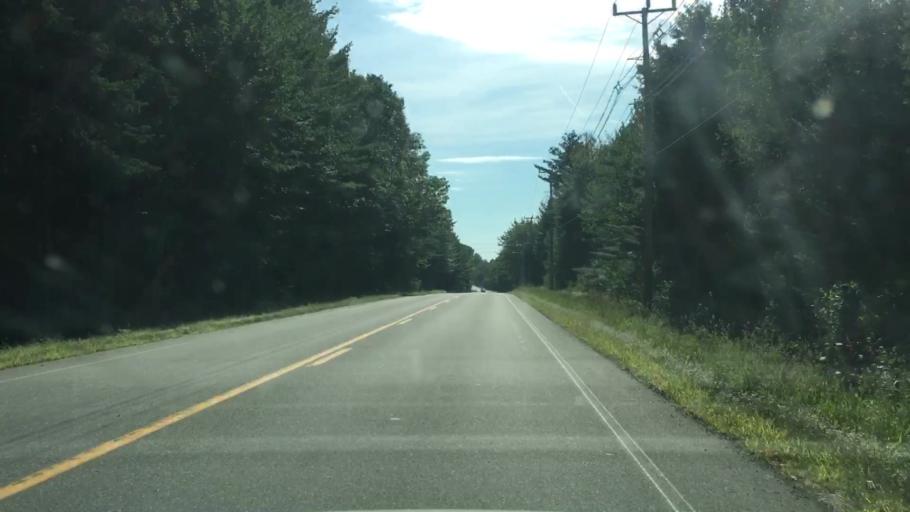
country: US
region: Maine
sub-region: Penobscot County
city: Lincoln
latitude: 45.3906
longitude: -68.5327
